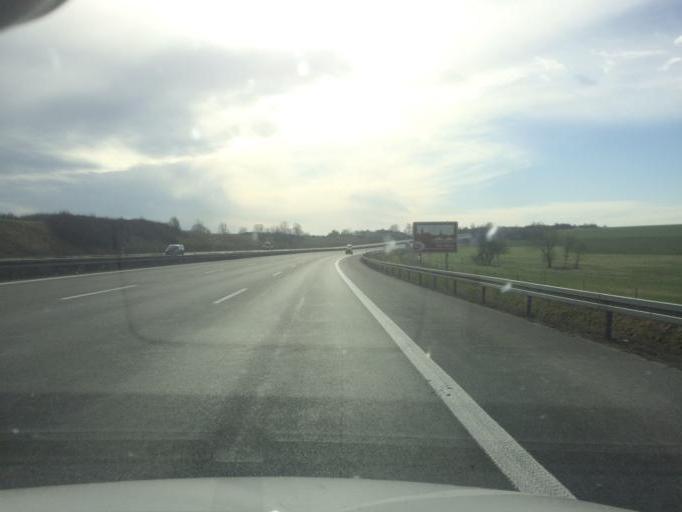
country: DE
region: Bavaria
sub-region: Upper Franconia
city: Berg
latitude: 50.3909
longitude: 11.7701
